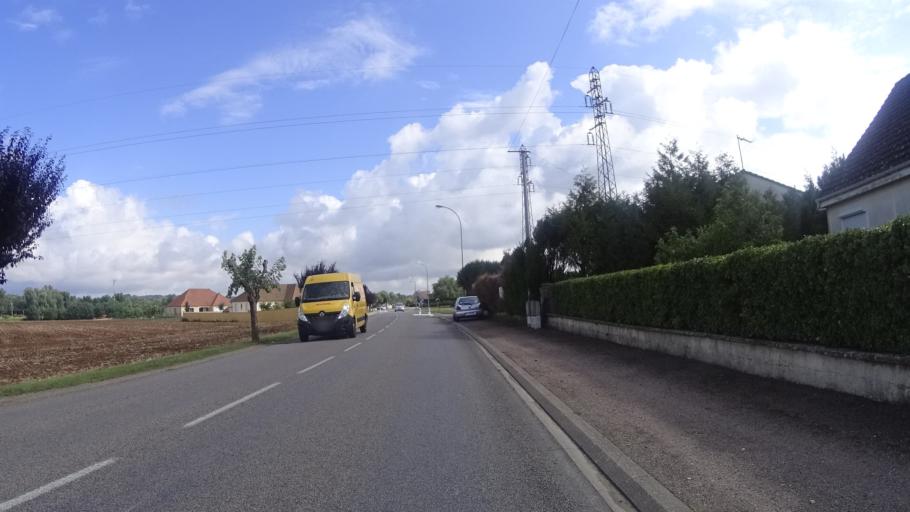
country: FR
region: Bourgogne
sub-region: Departement de l'Yonne
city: Vergigny
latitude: 47.9757
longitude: 3.7237
